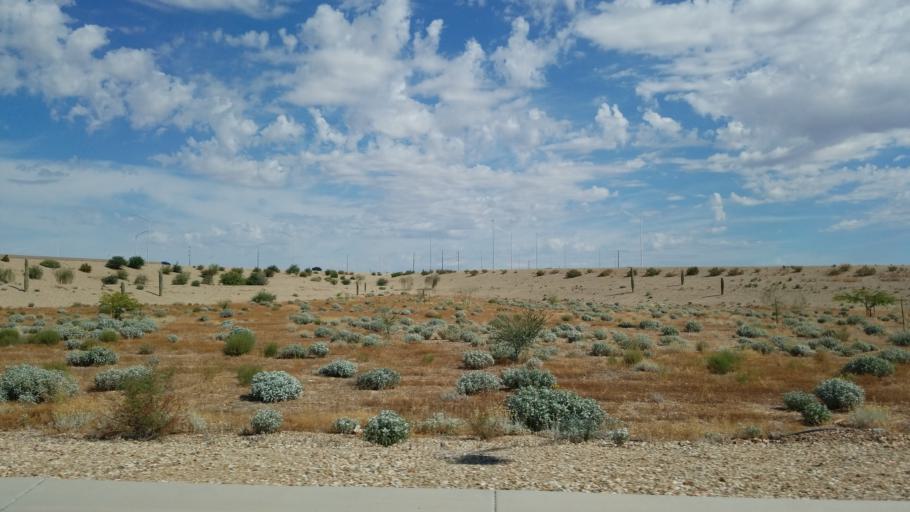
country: US
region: Arizona
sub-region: Maricopa County
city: Citrus Park
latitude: 33.5593
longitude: -112.4161
